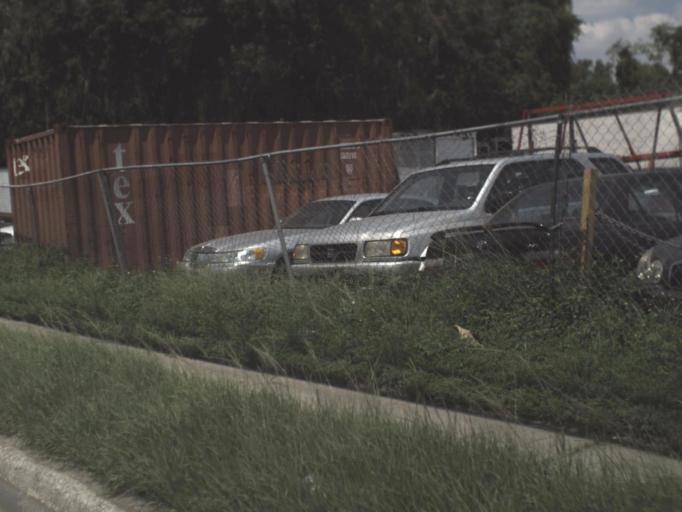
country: US
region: Florida
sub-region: Hillsborough County
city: Palm River-Clair Mel
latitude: 27.9306
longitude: -82.4018
